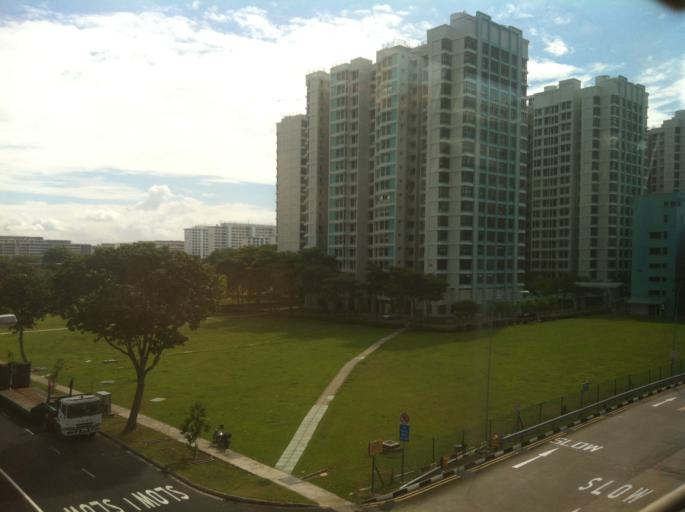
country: SG
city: Singapore
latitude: 1.3195
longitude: 103.9003
